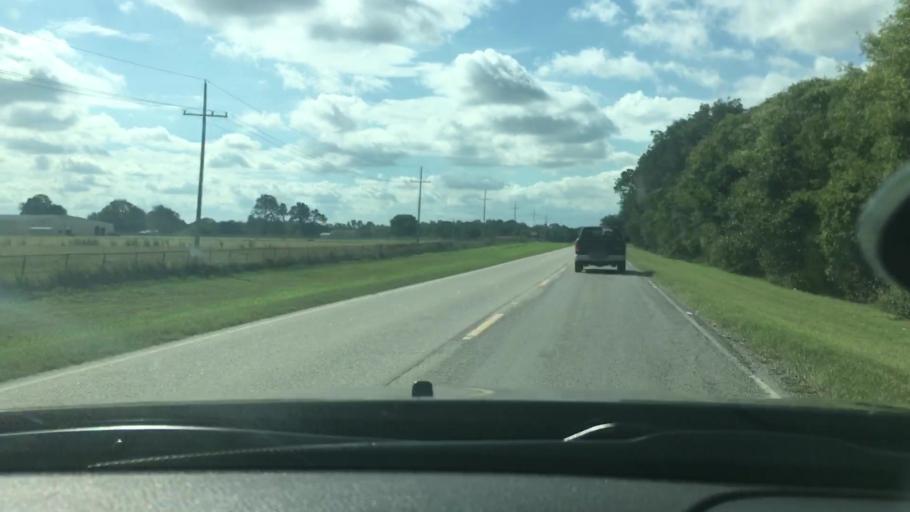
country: US
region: Oklahoma
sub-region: Pontotoc County
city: Ada
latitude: 34.6929
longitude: -96.6349
